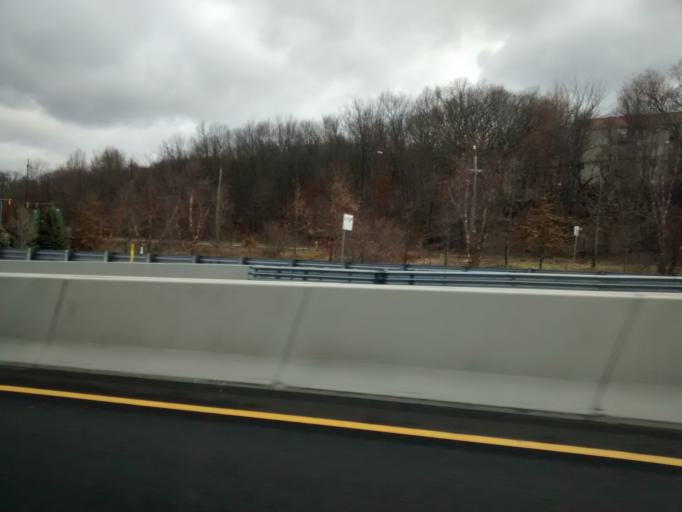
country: US
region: Massachusetts
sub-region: Worcester County
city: Sunderland
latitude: 42.2345
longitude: -71.7909
